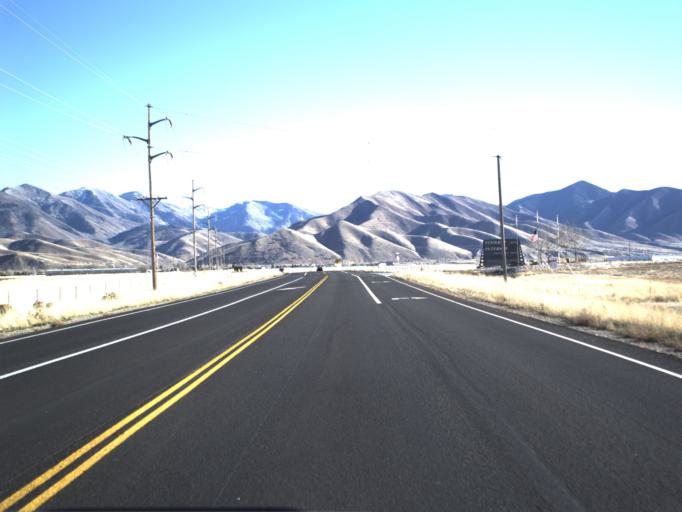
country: US
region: Utah
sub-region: Tooele County
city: Tooele
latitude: 40.5449
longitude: -112.3392
